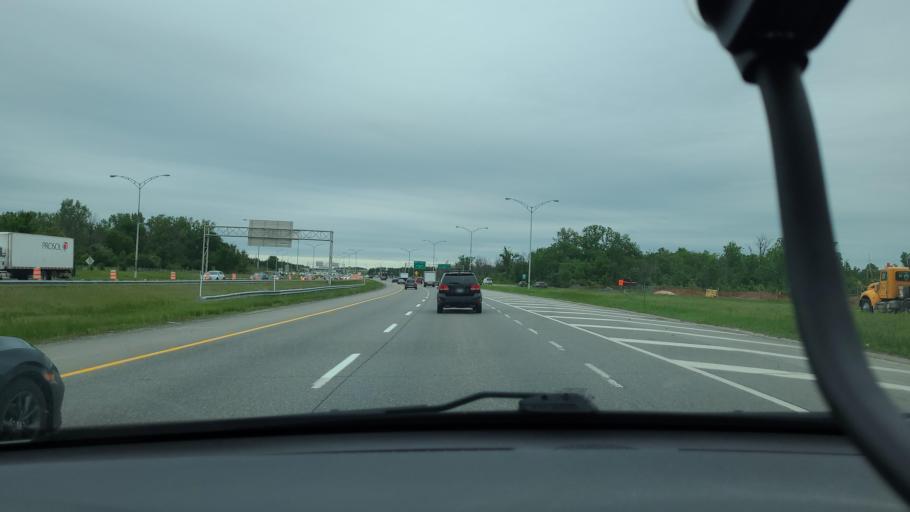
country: CA
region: Quebec
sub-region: Laval
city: Laval
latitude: 45.6206
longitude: -73.6648
